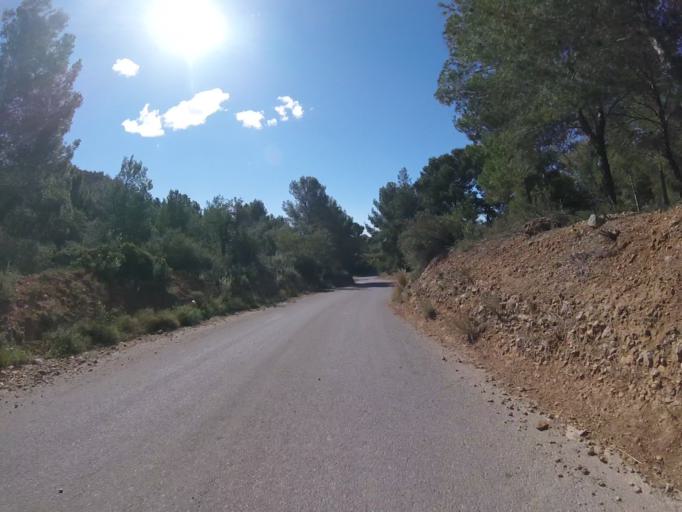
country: ES
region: Valencia
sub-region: Provincia de Castello
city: Benicassim
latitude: 40.0701
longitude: 0.0749
